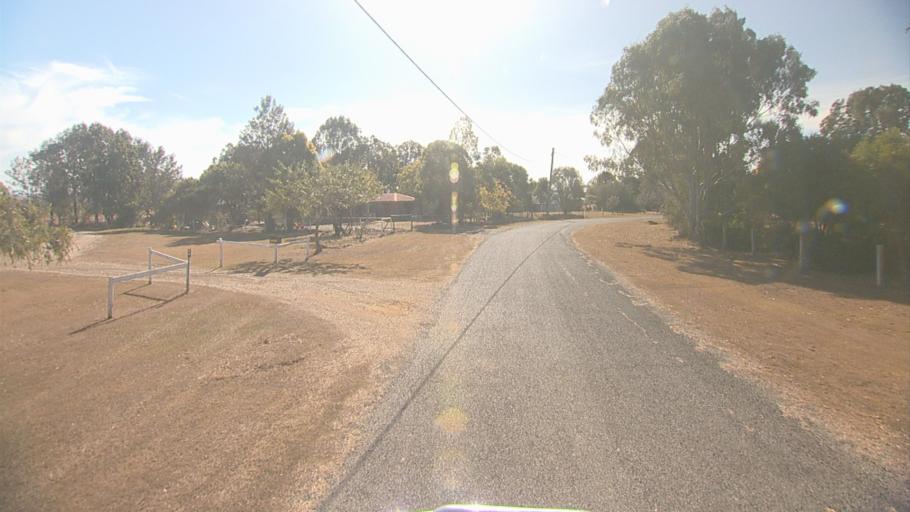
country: AU
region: Queensland
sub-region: Logan
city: Cedar Vale
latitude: -27.8690
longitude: 152.9643
